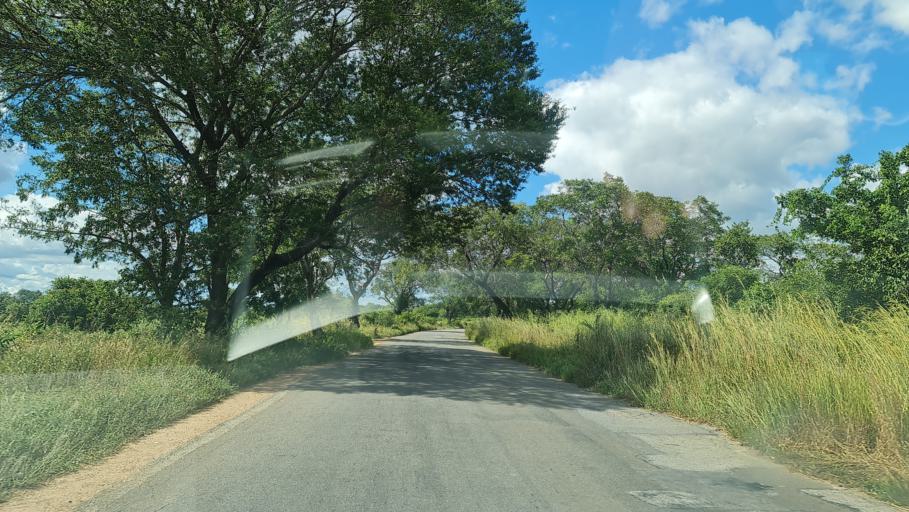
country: MZ
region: Zambezia
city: Quelimane
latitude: -17.5103
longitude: 36.2297
